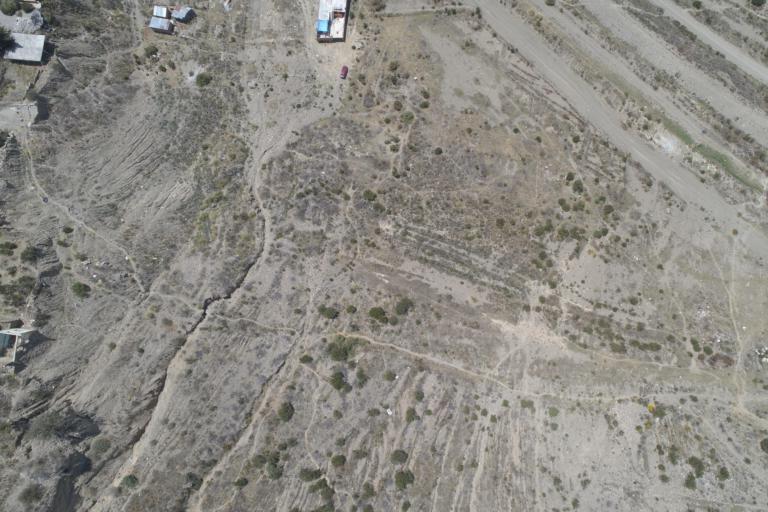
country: BO
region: La Paz
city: La Paz
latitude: -16.5021
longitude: -68.0998
